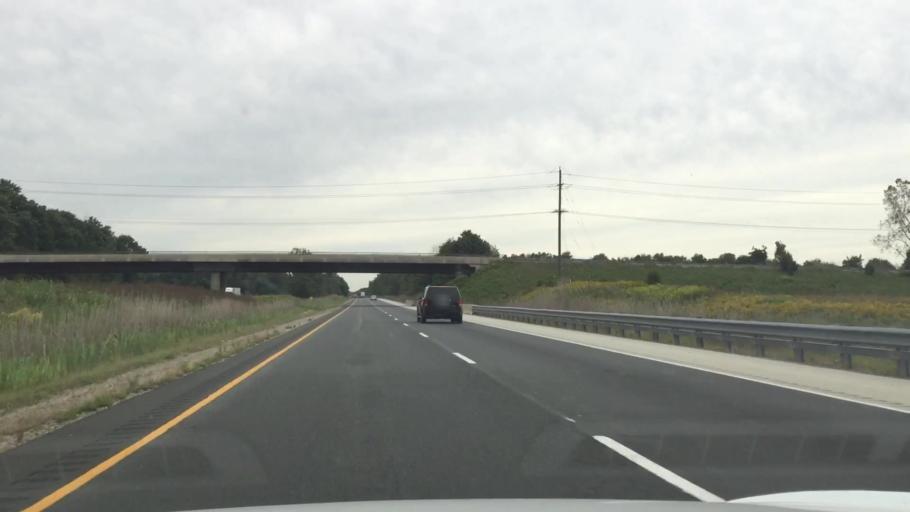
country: CA
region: Ontario
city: Camlachie
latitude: 42.9914
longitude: -82.0480
